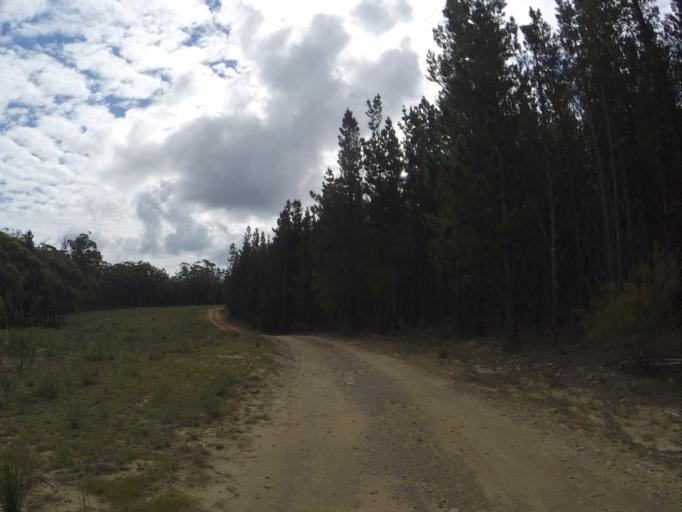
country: AU
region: New South Wales
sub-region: Wingecarribee
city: Moss Vale
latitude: -34.5161
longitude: 150.2275
